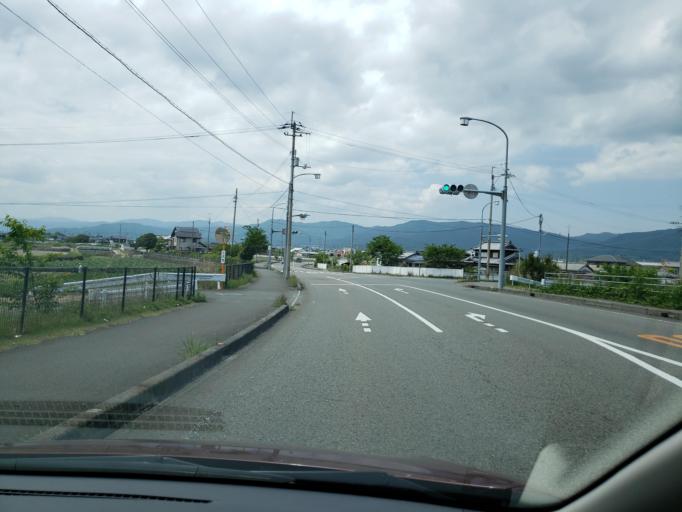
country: JP
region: Tokushima
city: Kamojimacho-jogejima
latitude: 34.0957
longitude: 134.3827
